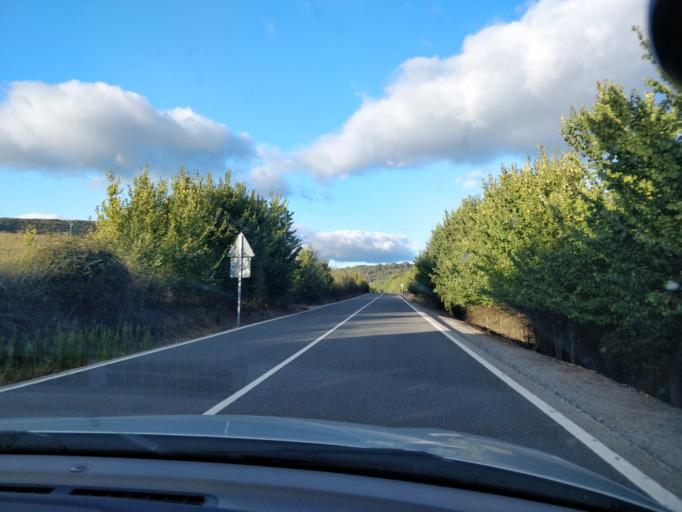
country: ES
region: Castille and Leon
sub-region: Provincia de Leon
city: Borrenes
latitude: 42.4946
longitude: -6.7395
